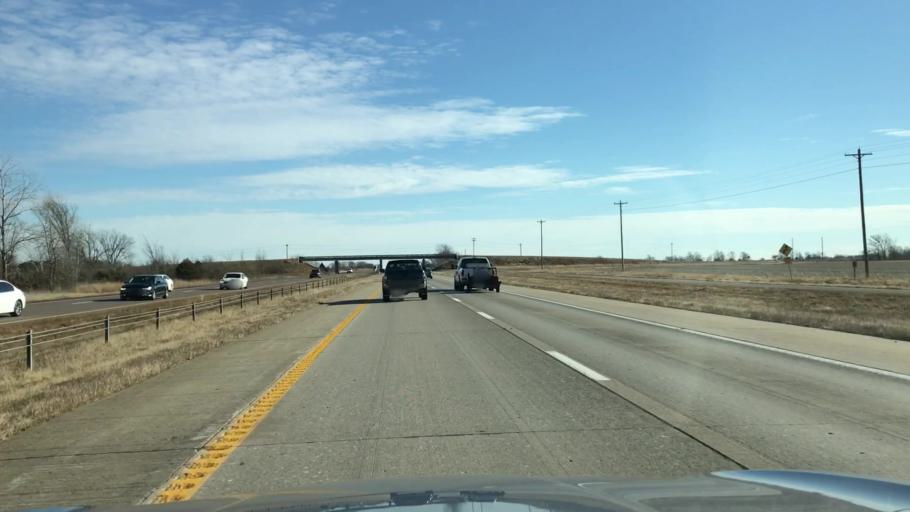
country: US
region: Missouri
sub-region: Callaway County
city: Fulton
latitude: 38.9178
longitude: -91.7470
